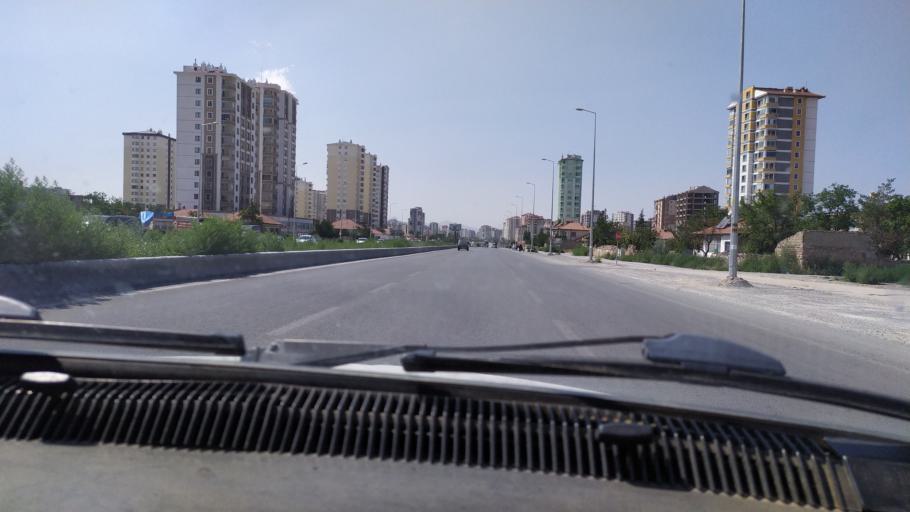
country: TR
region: Kayseri
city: Talas
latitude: 38.7204
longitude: 35.5454
